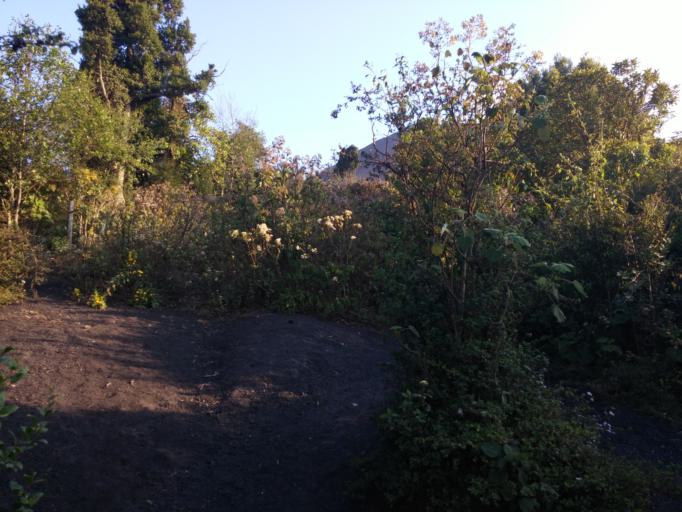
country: GT
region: Escuintla
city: San Vicente Pacaya
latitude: 14.3920
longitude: -90.5994
